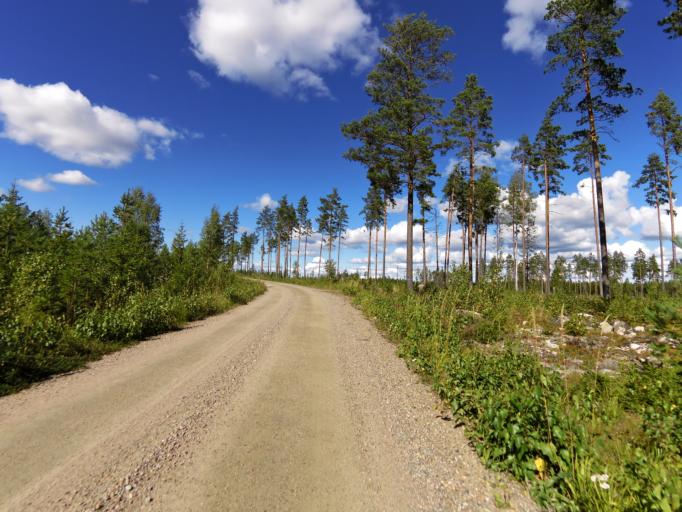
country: SE
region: Gaevleborg
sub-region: Ockelbo Kommun
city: Ockelbo
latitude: 60.7997
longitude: 16.8668
